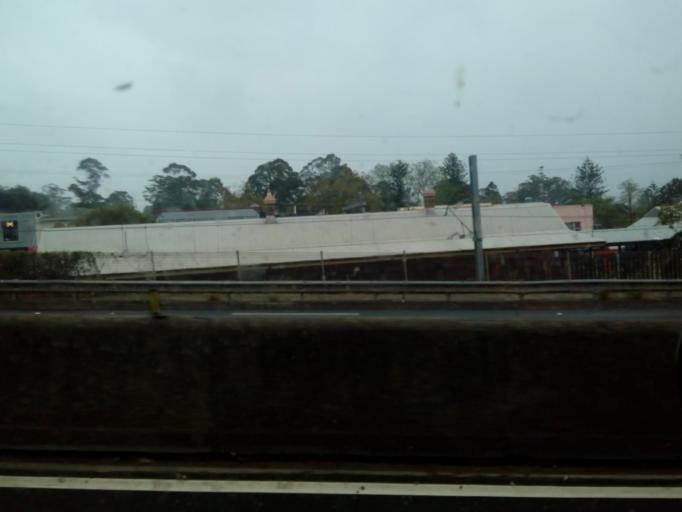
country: AU
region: New South Wales
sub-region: City of Sydney
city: Pymble
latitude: -33.7449
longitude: 151.1418
